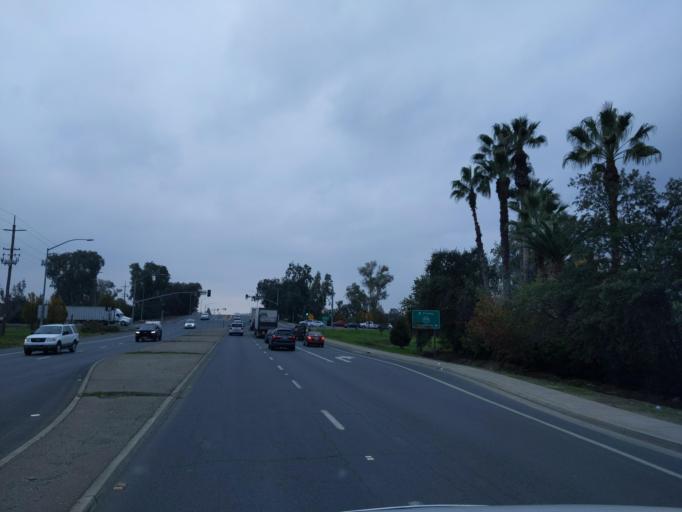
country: US
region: California
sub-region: San Joaquin County
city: Garden Acres
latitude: 37.9710
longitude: -121.2432
